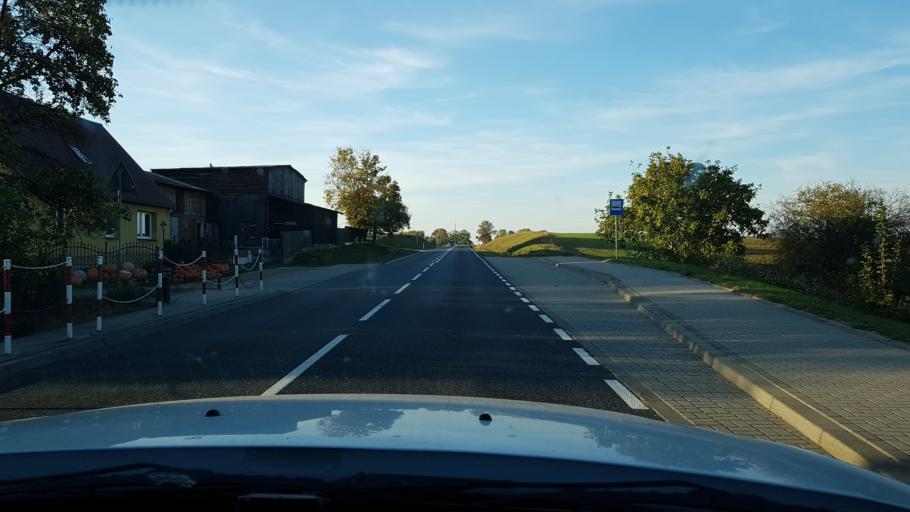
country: DE
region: Brandenburg
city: Schwedt (Oder)
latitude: 53.0262
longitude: 14.3230
